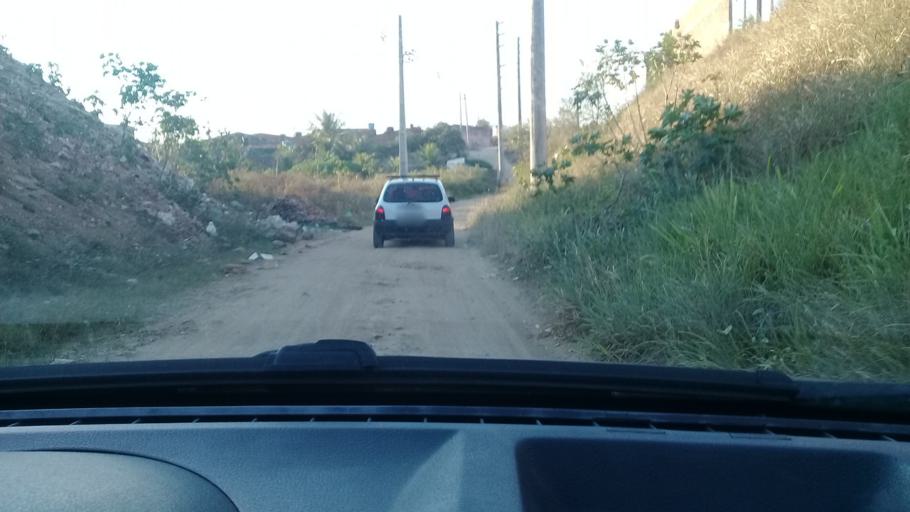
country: BR
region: Pernambuco
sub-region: Vitoria De Santo Antao
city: Vitoria de Santo Antao
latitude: -8.1341
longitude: -35.2912
